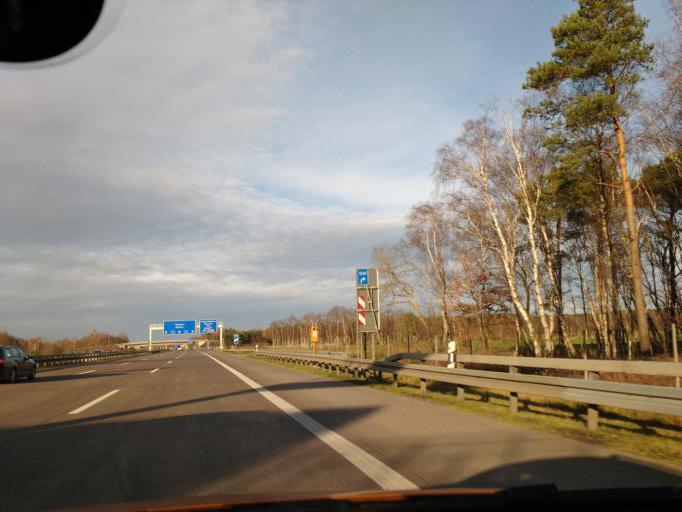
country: DE
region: Lower Saxony
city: Isernhagen Farster Bauerschaft
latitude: 52.4203
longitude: 9.8917
